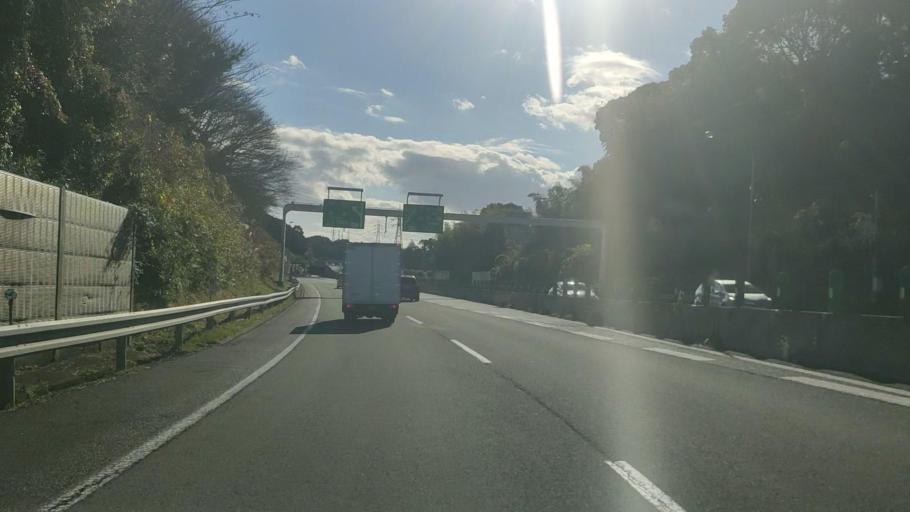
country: JP
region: Fukuoka
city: Kitakyushu
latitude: 33.8489
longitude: 130.7671
